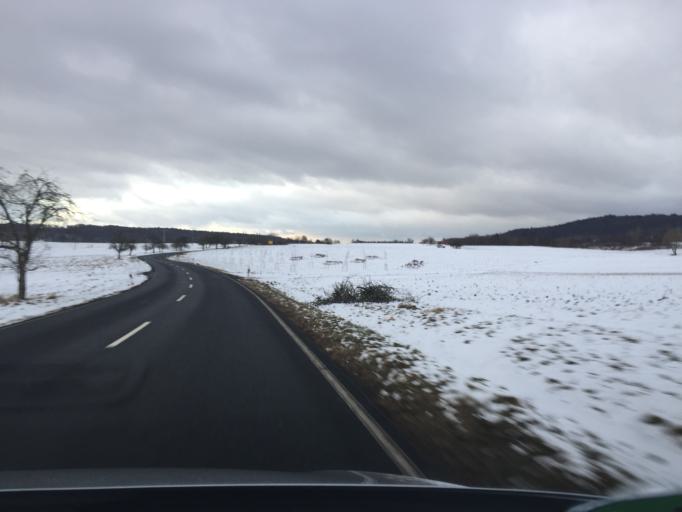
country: DE
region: Bavaria
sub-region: Regierungsbezirk Unterfranken
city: Geiselbach
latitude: 50.1148
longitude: 9.2079
